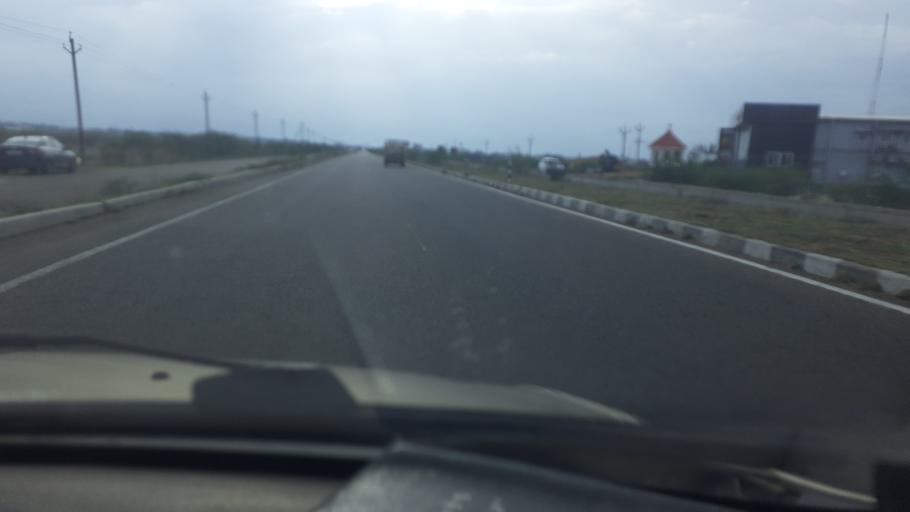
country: IN
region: Tamil Nadu
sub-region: Tirunelveli Kattabo
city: Tirunelveli
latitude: 8.6649
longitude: 77.7336
